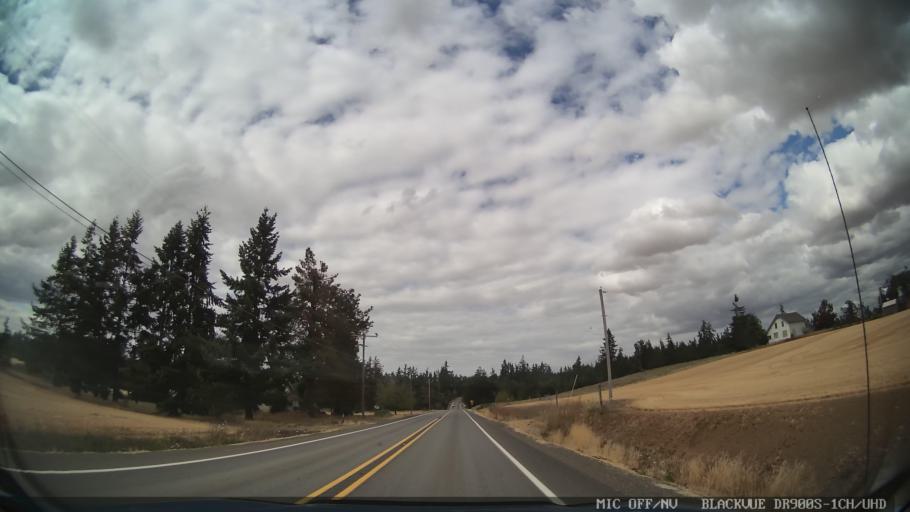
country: US
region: Oregon
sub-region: Marion County
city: Sublimity
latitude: 44.8451
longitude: -122.7945
